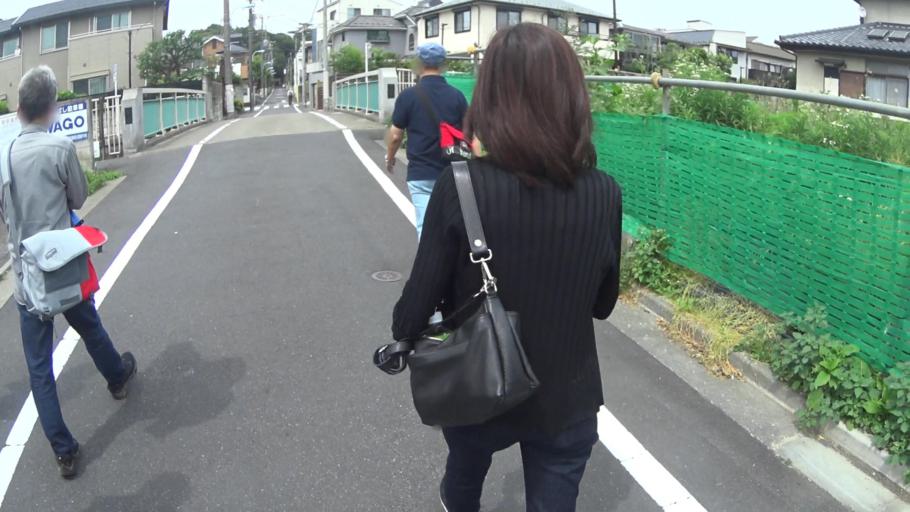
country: JP
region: Tokyo
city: Musashino
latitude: 35.7084
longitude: 139.6059
